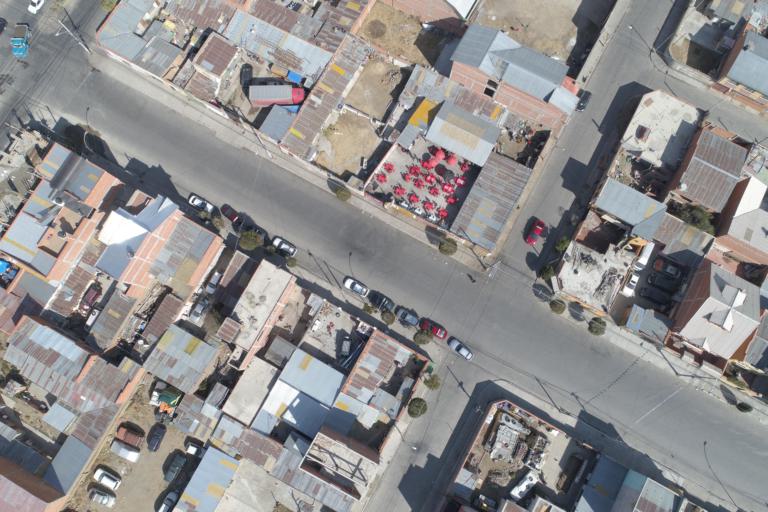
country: BO
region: La Paz
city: La Paz
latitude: -16.5275
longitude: -68.1471
